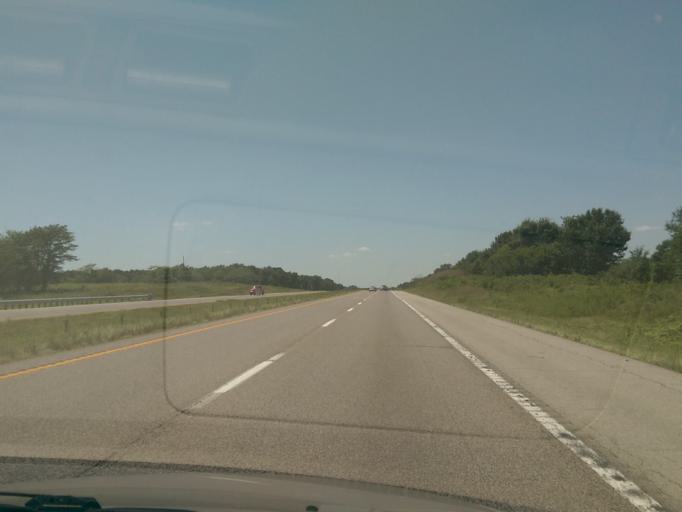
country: US
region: Missouri
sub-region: Saline County
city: Marshall
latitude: 38.9509
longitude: -93.0544
